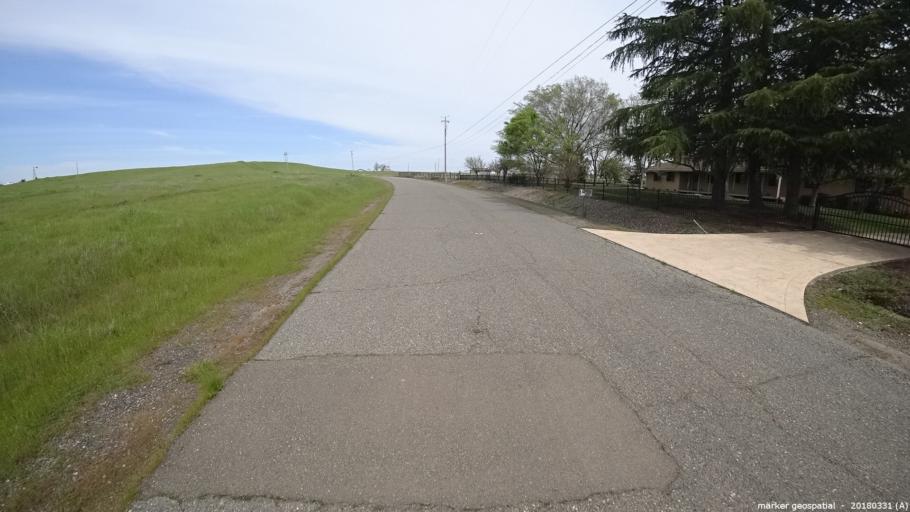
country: US
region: California
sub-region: Sacramento County
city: Rancho Murieta
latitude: 38.4879
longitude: -121.1343
